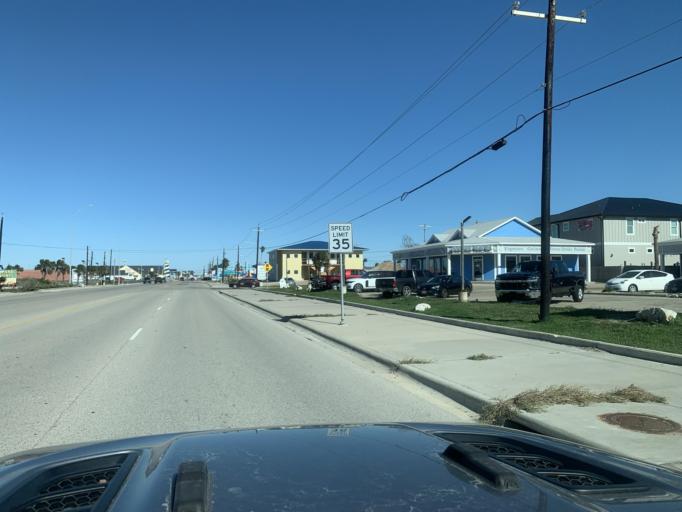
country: US
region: Texas
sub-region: Nueces County
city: Port Aransas
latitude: 27.8254
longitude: -97.0693
